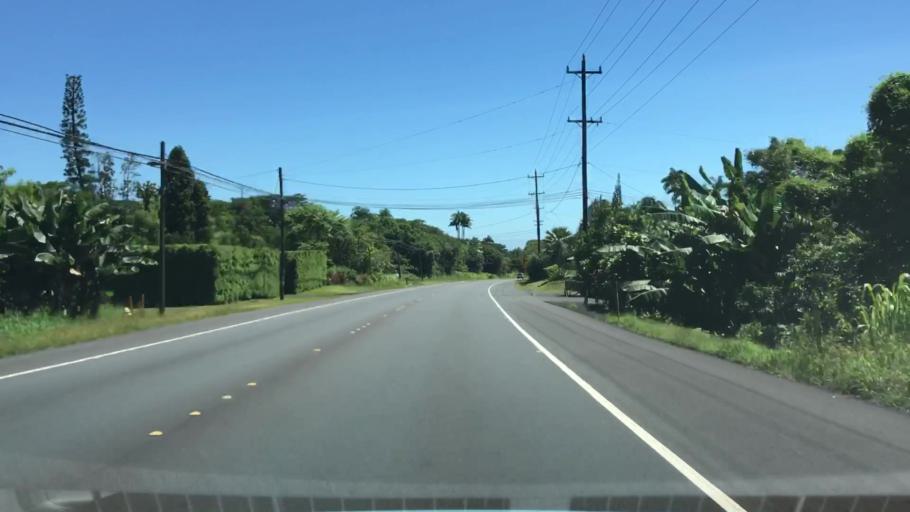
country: US
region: Hawaii
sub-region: Hawaii County
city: Mountain View
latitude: 19.5711
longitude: -155.0782
